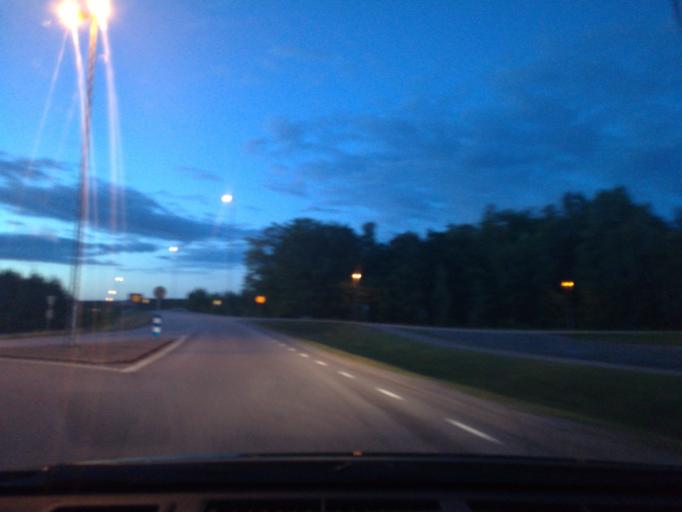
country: SE
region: Uppsala
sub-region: Habo Kommun
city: Balsta
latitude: 59.5842
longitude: 17.5068
